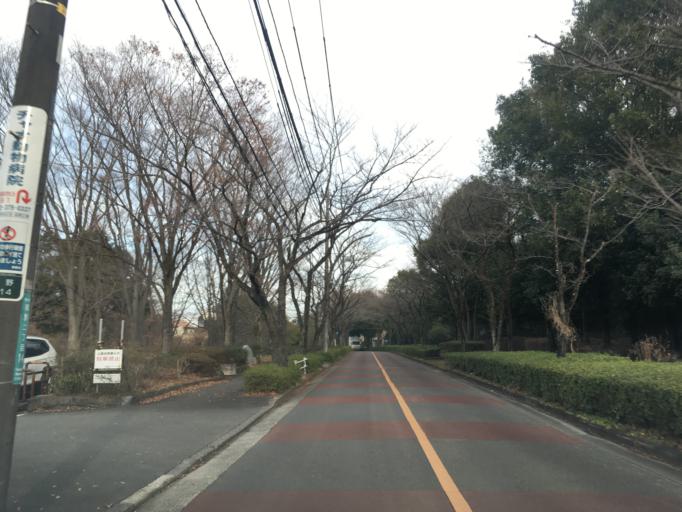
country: JP
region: Tokyo
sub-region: Machida-shi
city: Machida
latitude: 35.6067
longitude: 139.4330
